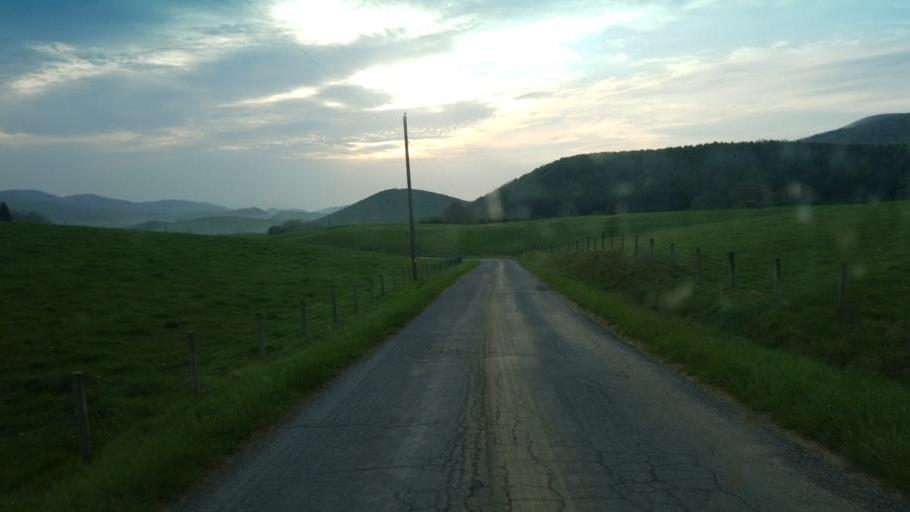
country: US
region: Virginia
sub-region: Smyth County
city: Marion
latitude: 36.7622
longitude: -81.4604
